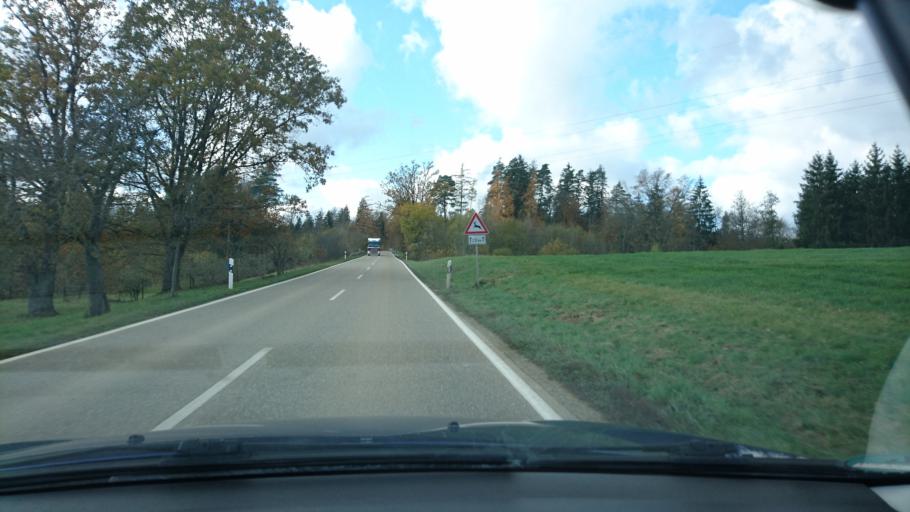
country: DE
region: Baden-Wuerttemberg
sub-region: Regierungsbezirk Stuttgart
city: Abtsgmund
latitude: 48.8907
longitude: 9.9890
